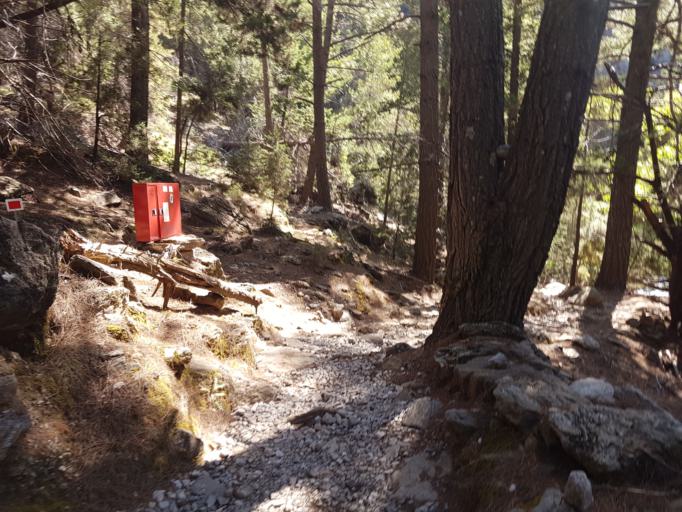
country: GR
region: Crete
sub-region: Nomos Chanias
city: Perivolia
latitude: 35.3062
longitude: 23.9383
